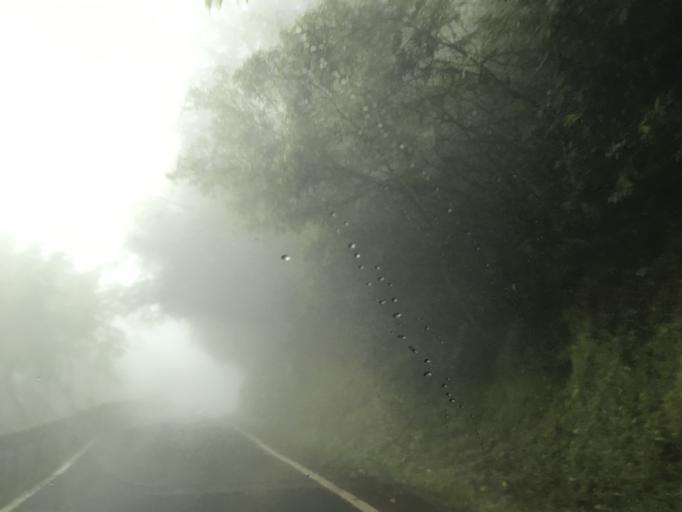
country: TW
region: Taiwan
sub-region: Hualien
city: Hualian
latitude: 24.1894
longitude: 121.4204
